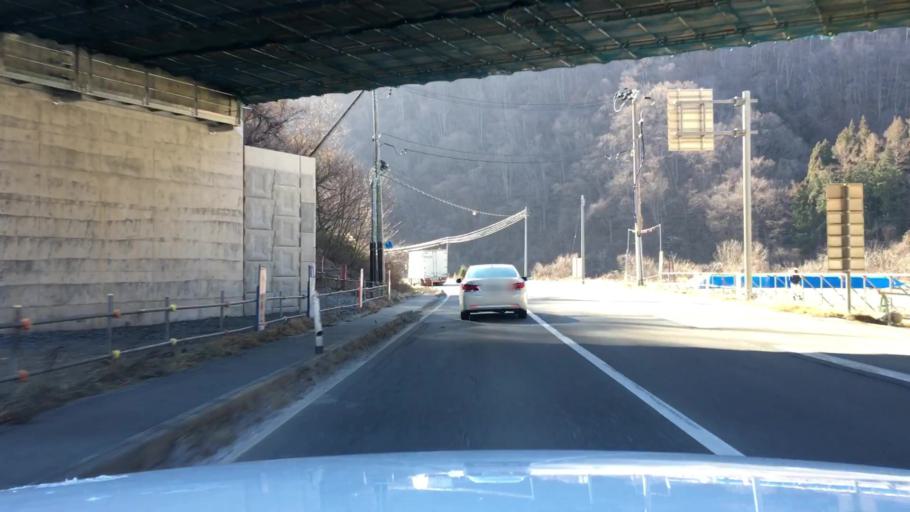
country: JP
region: Iwate
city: Miyako
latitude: 39.5997
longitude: 141.6475
